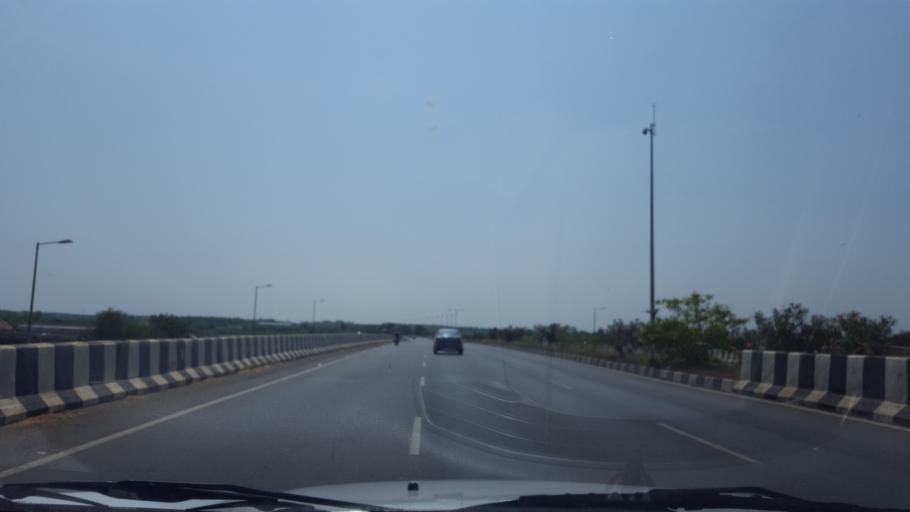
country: IN
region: Andhra Pradesh
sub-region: Prakasam
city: Ongole
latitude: 15.3903
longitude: 80.0394
